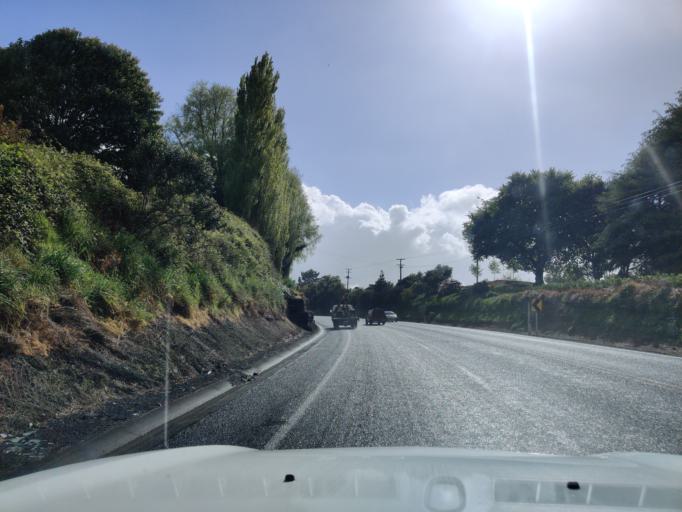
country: NZ
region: Waikato
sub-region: Matamata-Piako District
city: Matamata
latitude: -37.9468
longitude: 175.6559
